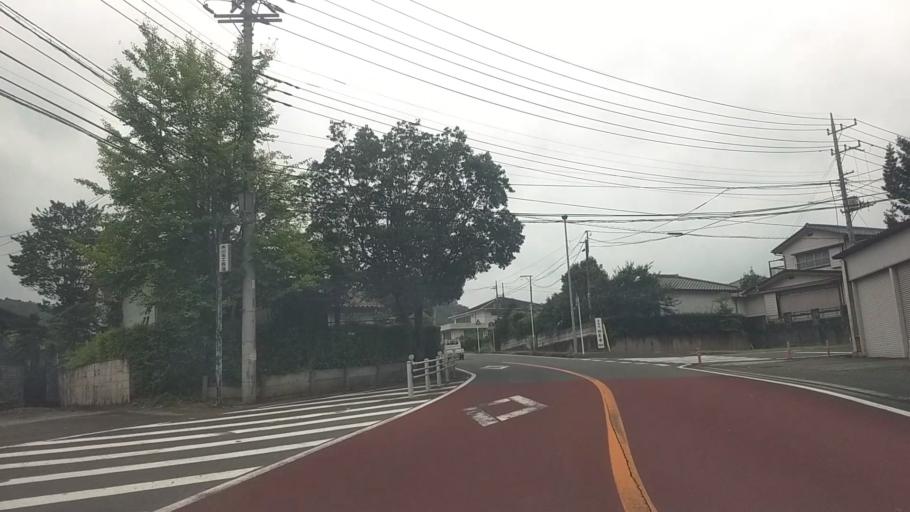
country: JP
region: Chiba
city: Kisarazu
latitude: 35.2890
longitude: 140.0837
